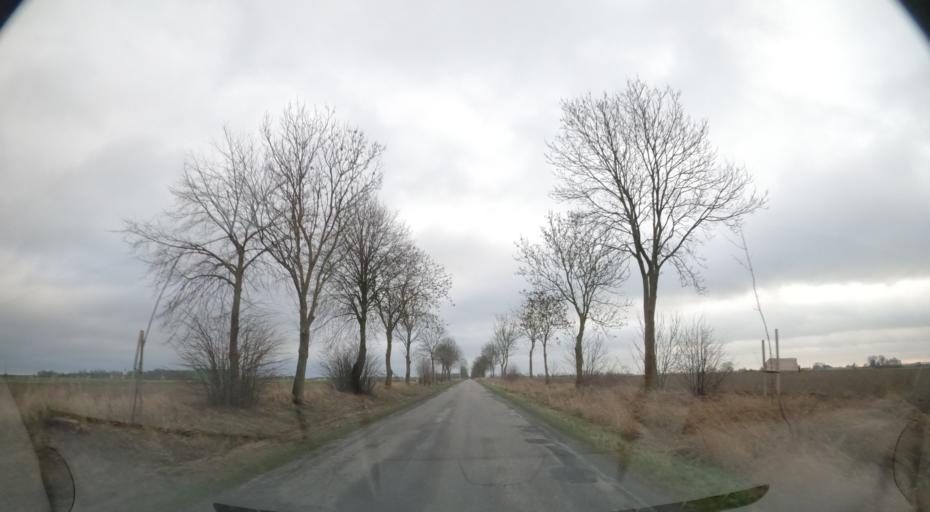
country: PL
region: Greater Poland Voivodeship
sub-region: Powiat pilski
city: Lobzenica
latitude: 53.2642
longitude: 17.2196
